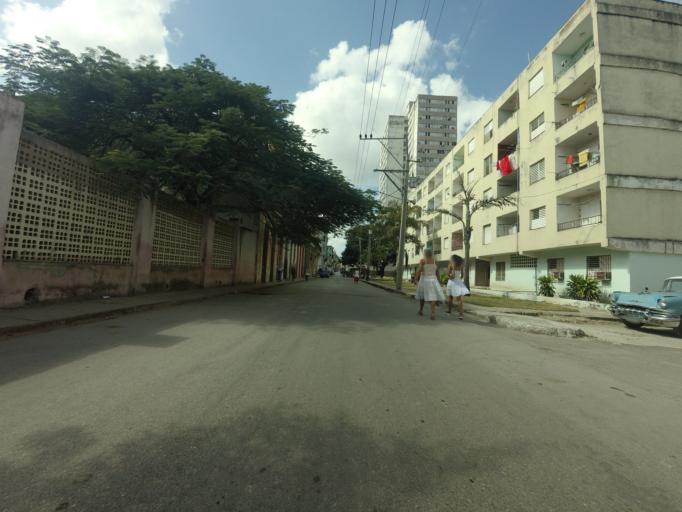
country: CU
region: La Habana
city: Havana
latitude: 23.1351
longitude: -82.3750
